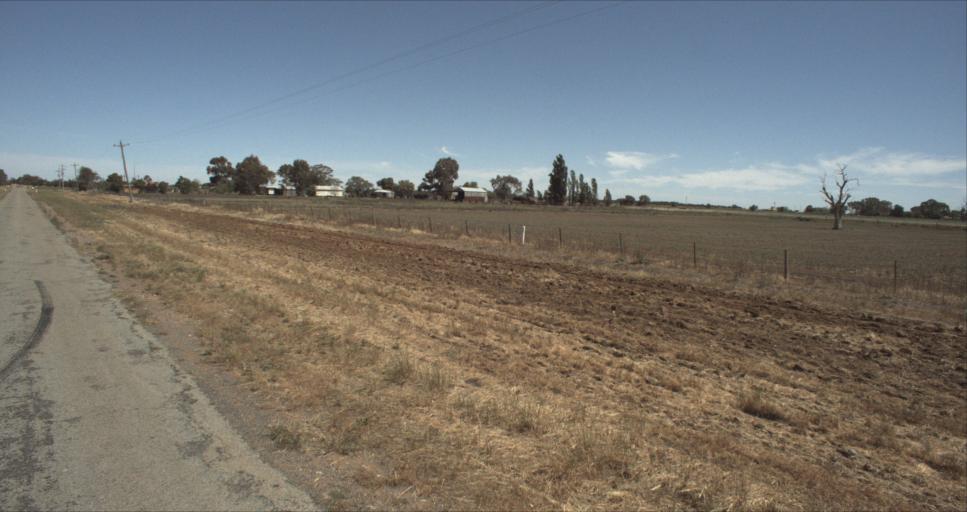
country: AU
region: New South Wales
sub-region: Leeton
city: Leeton
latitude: -34.5085
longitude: 146.3446
